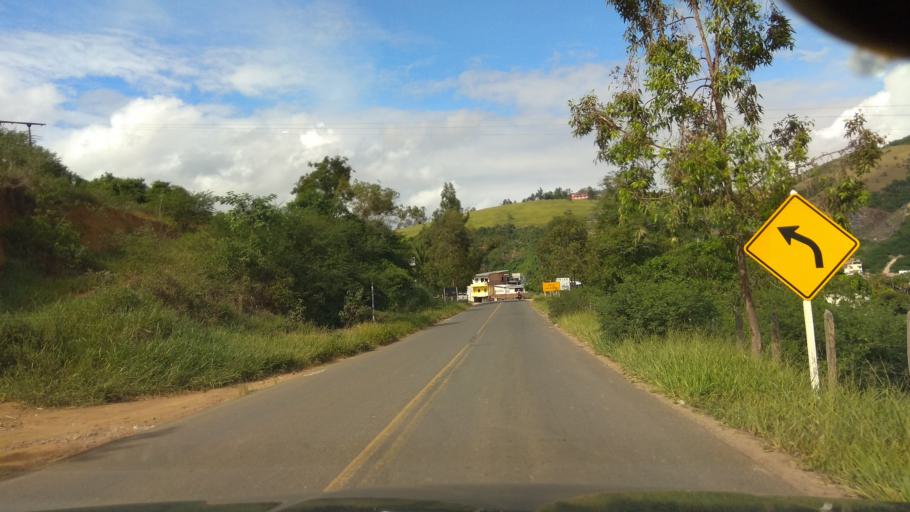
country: BR
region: Bahia
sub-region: Ubaira
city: Ubaira
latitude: -13.2676
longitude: -39.6590
